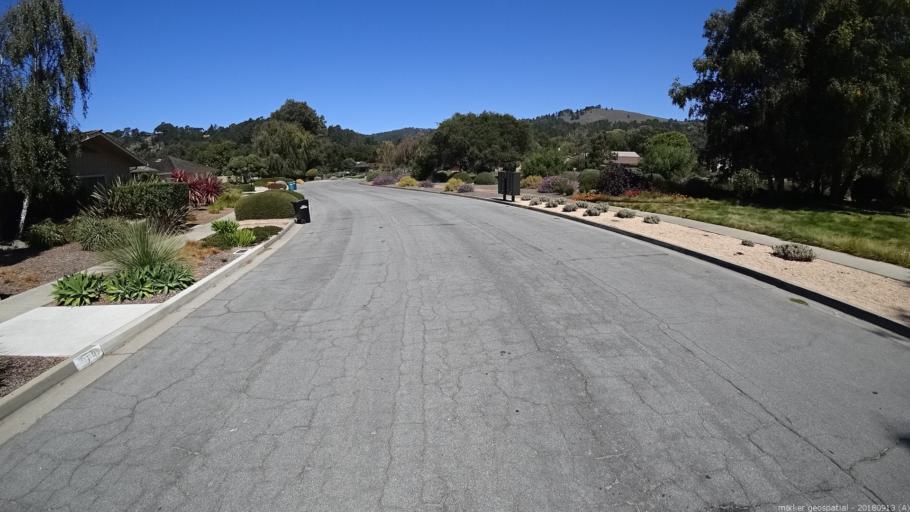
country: US
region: California
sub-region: Monterey County
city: Carmel-by-the-Sea
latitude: 36.5353
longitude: -121.8686
